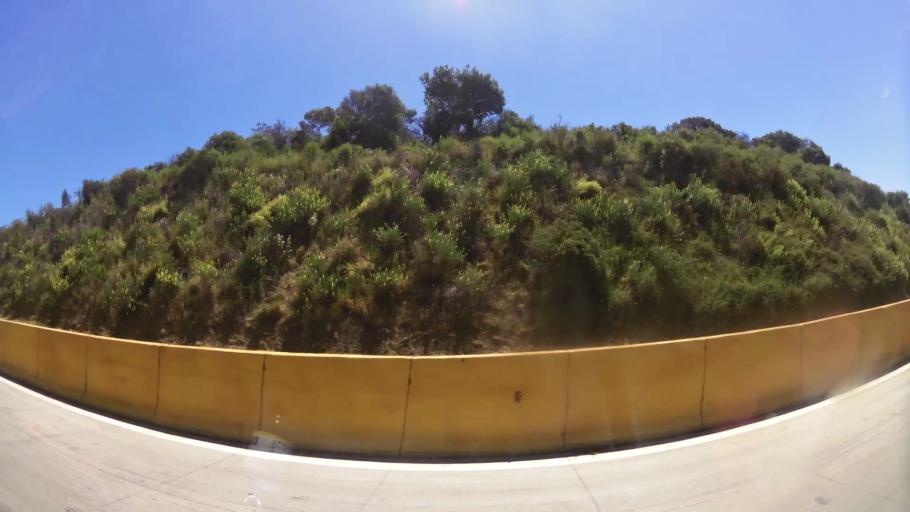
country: CL
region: Valparaiso
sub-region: Provincia de Valparaiso
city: Valparaiso
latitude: -33.0627
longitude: -71.6415
